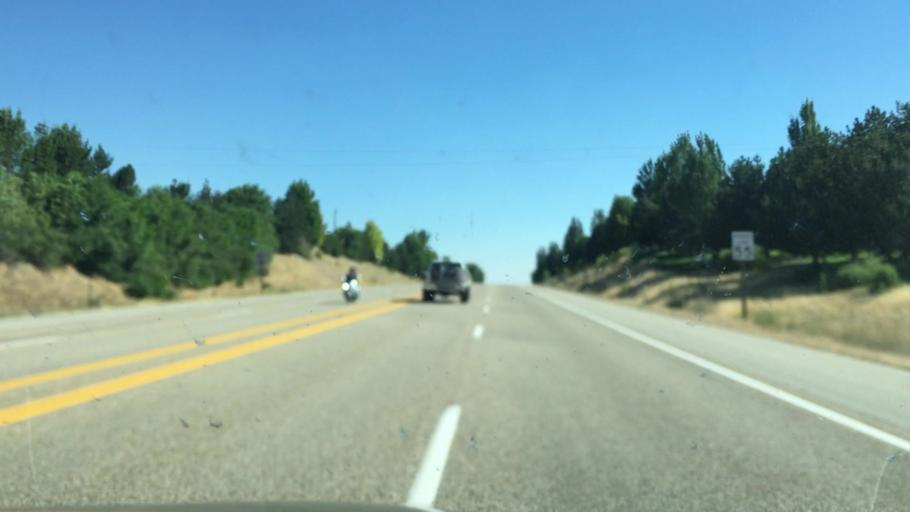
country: US
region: Idaho
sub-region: Ada County
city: Eagle
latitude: 43.7178
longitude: -116.3196
